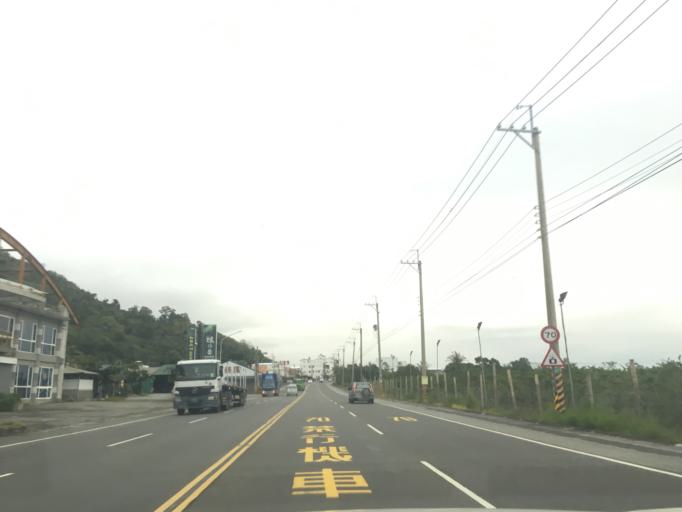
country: TW
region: Taiwan
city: Taitung City
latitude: 22.6816
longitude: 121.0427
